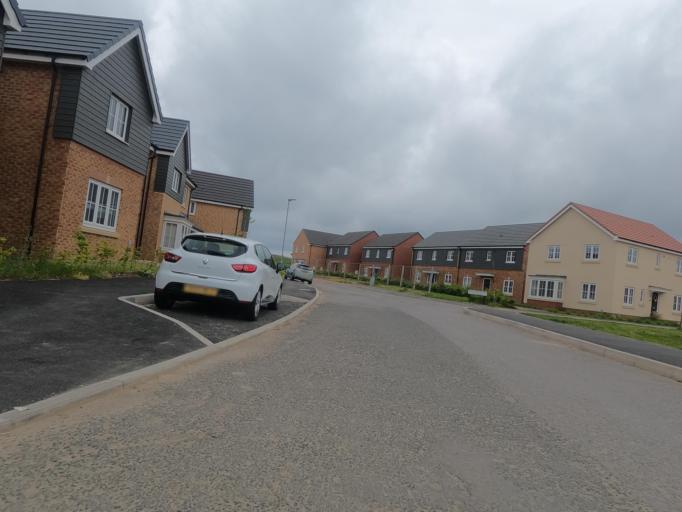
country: GB
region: England
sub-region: Northumberland
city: Seaton Delaval
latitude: 55.1044
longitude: -1.5347
